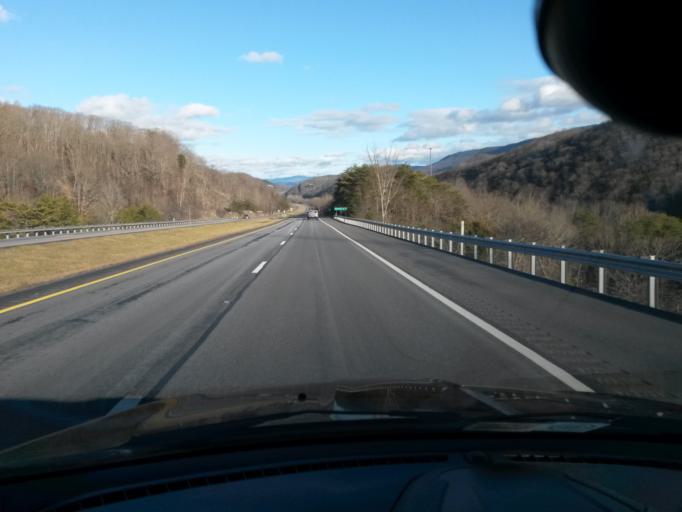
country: US
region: West Virginia
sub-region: Mercer County
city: Athens
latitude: 37.3462
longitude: -80.9284
